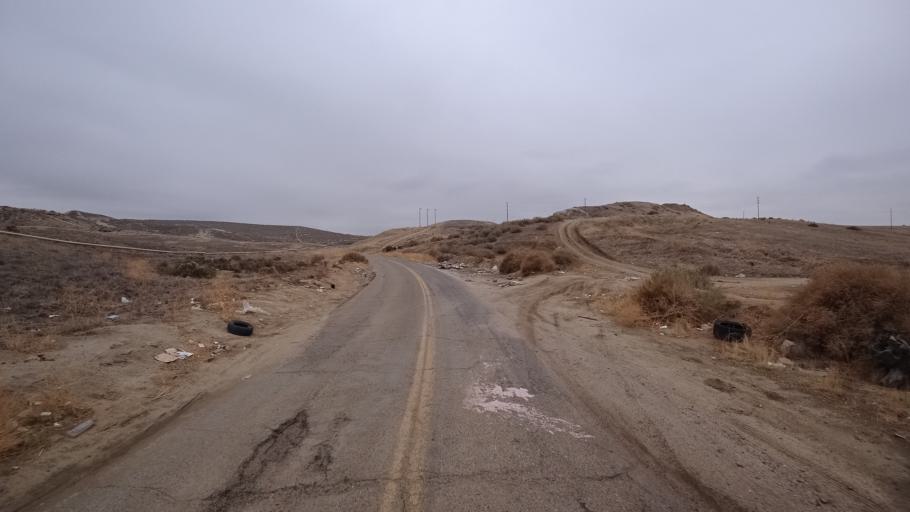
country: US
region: California
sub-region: Kern County
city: Oildale
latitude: 35.4232
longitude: -118.9385
